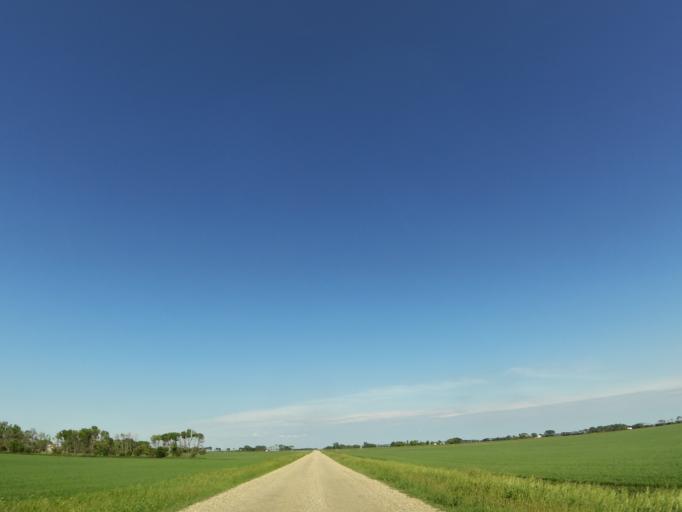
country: US
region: North Dakota
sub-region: Walsh County
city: Grafton
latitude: 48.3535
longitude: -97.2549
